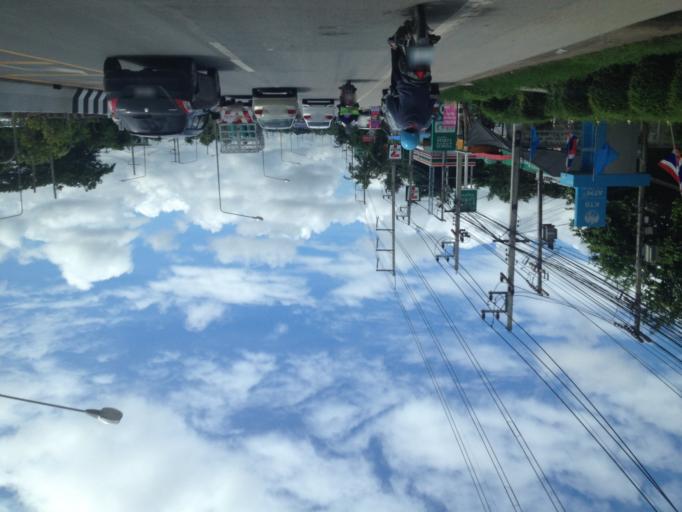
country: TH
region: Chiang Mai
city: Chiang Mai
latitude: 18.7695
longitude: 98.9501
